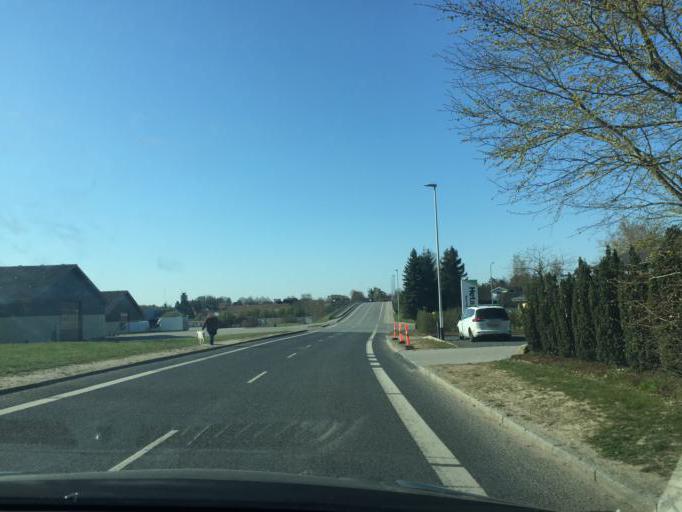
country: DK
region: South Denmark
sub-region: Faaborg-Midtfyn Kommune
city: Ringe
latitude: 55.2465
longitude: 10.4858
